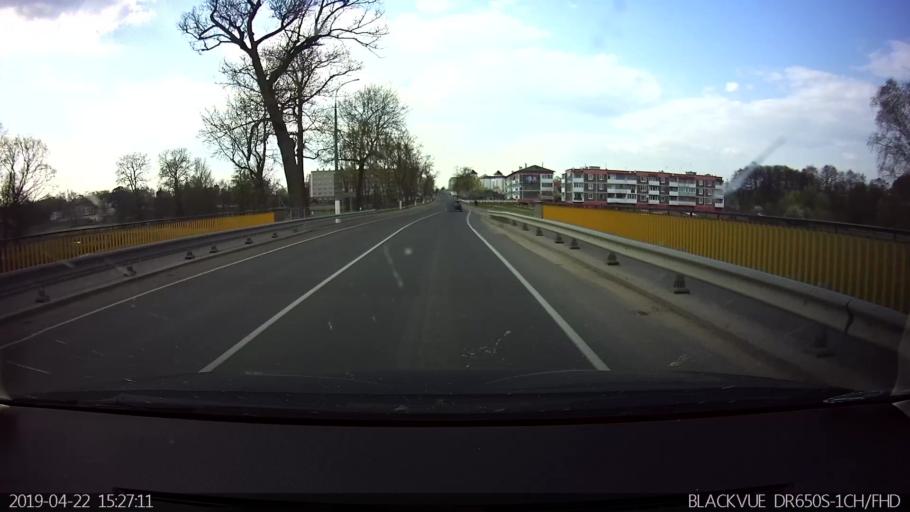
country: BY
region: Brest
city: Vysokaye
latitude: 52.3693
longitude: 23.3742
